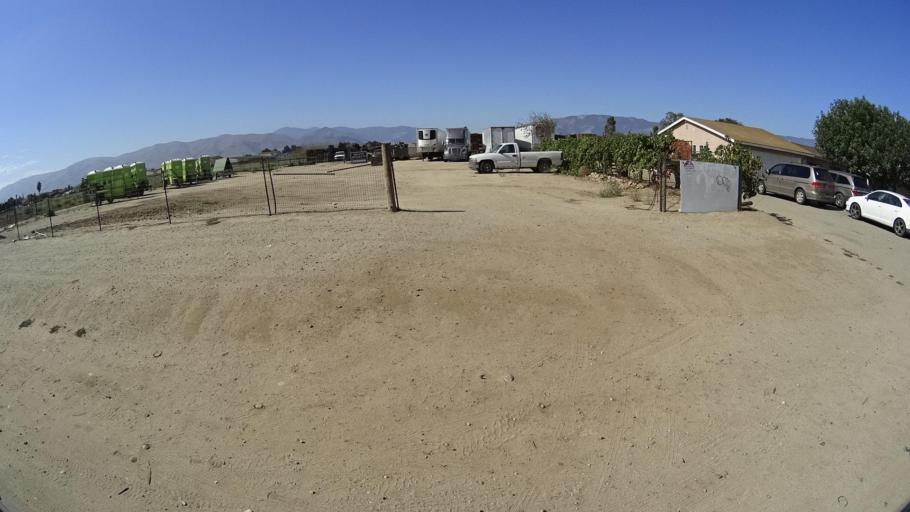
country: US
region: California
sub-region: Monterey County
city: Greenfield
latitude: 36.3216
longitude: -121.2548
